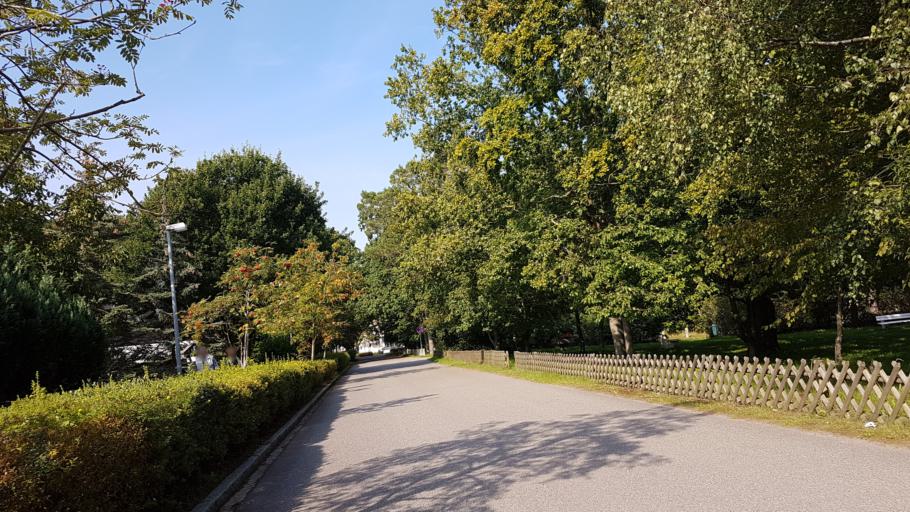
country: DE
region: Mecklenburg-Vorpommern
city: Glowe
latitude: 54.5666
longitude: 13.4591
